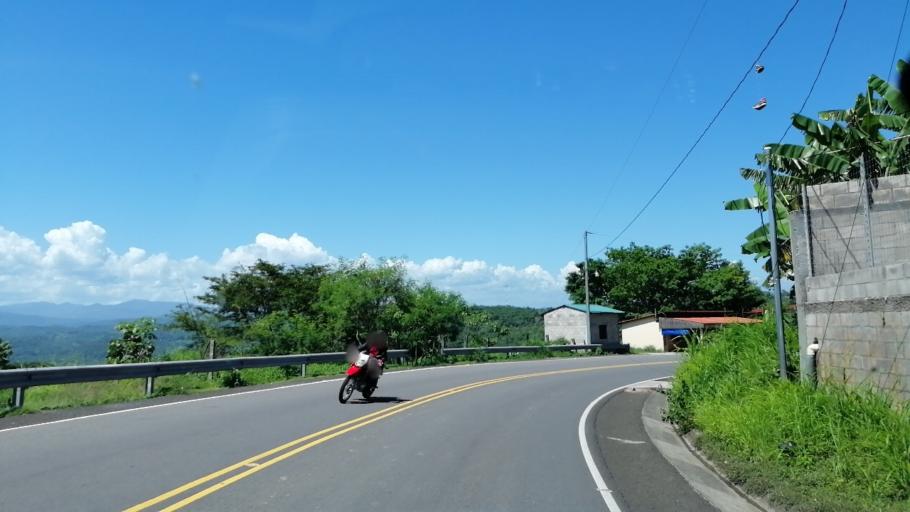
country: SV
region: Morazan
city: Cacaopera
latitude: 13.8100
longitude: -88.1543
